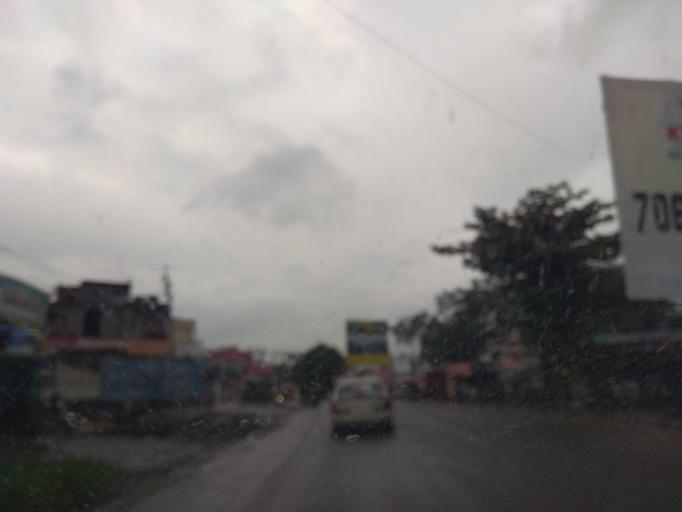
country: IN
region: Maharashtra
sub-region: Pune Division
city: Kharakvasla
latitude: 18.5109
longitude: 73.6884
